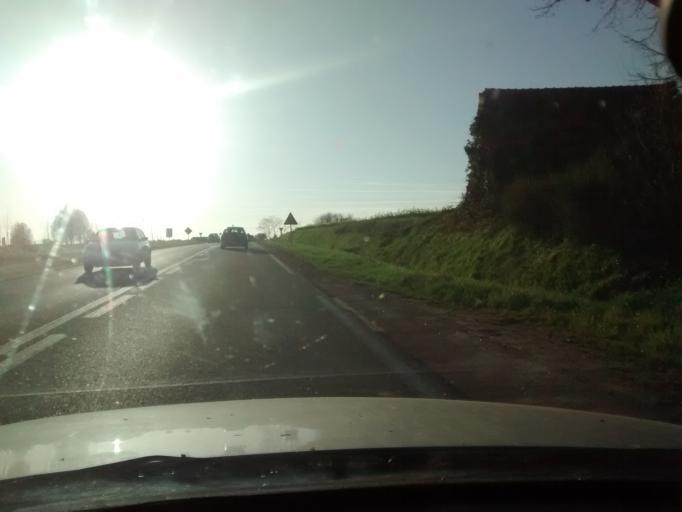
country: FR
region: Pays de la Loire
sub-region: Departement de la Sarthe
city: Trange
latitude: 48.0208
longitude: 0.1116
